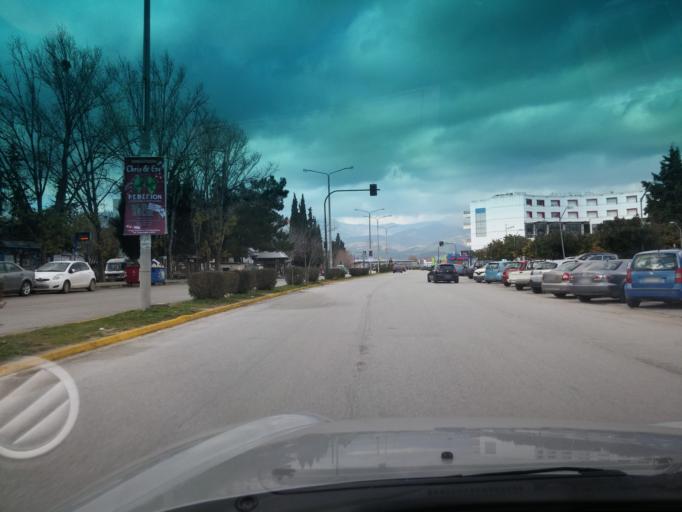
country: GR
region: East Macedonia and Thrace
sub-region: Nomos Rodopis
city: Komotini
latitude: 41.1244
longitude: 25.3944
